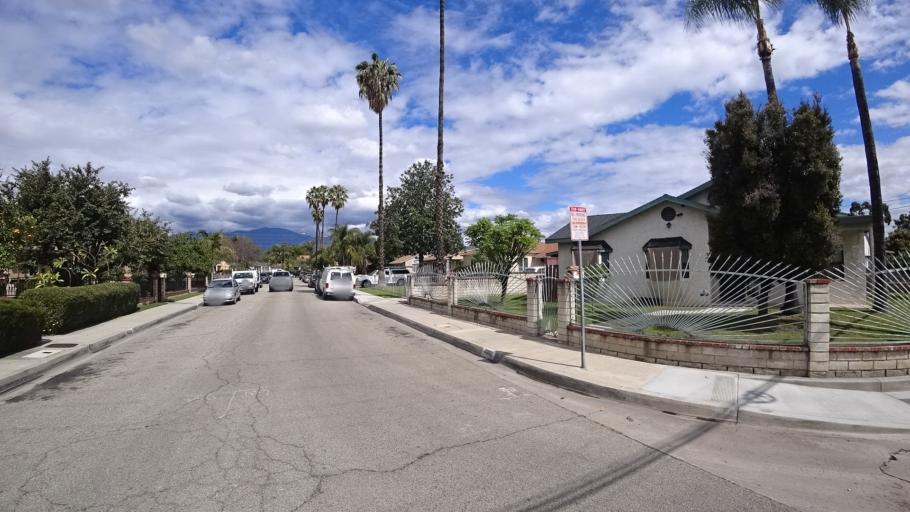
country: US
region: California
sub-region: Los Angeles County
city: Baldwin Park
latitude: 34.0905
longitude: -117.9639
